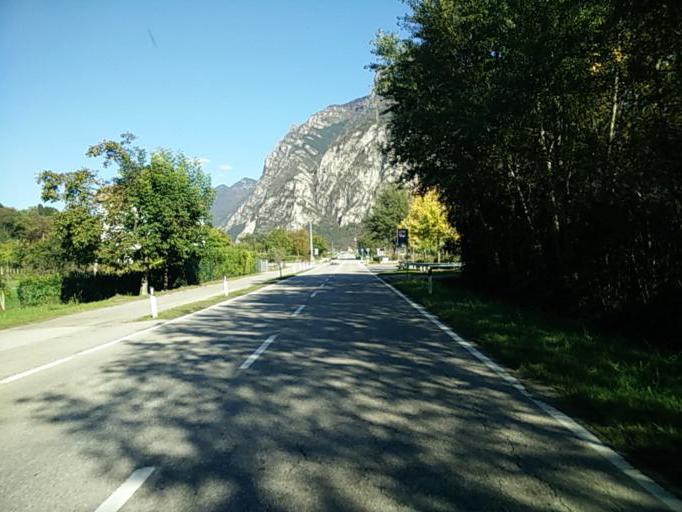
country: IT
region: Trentino-Alto Adige
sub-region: Provincia di Trento
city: Storo
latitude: 45.8489
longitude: 10.5589
